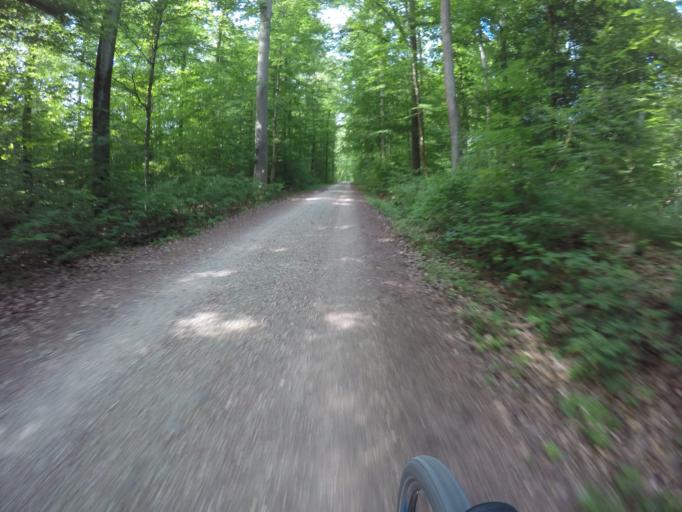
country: DE
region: Baden-Wuerttemberg
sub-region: Regierungsbezirk Stuttgart
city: Denkendorf
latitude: 48.6762
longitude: 9.3178
